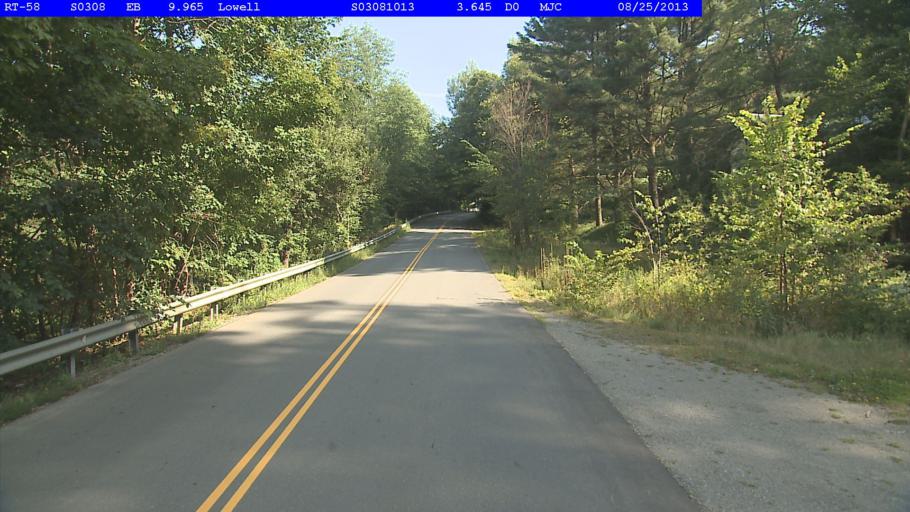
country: US
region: Vermont
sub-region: Lamoille County
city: Hyde Park
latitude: 44.8031
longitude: -72.4558
